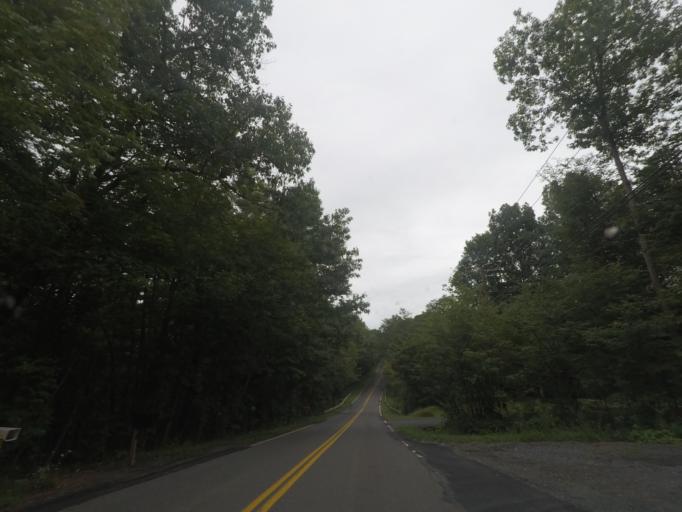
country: US
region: New York
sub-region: Columbia County
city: Chatham
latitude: 42.4157
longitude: -73.5367
